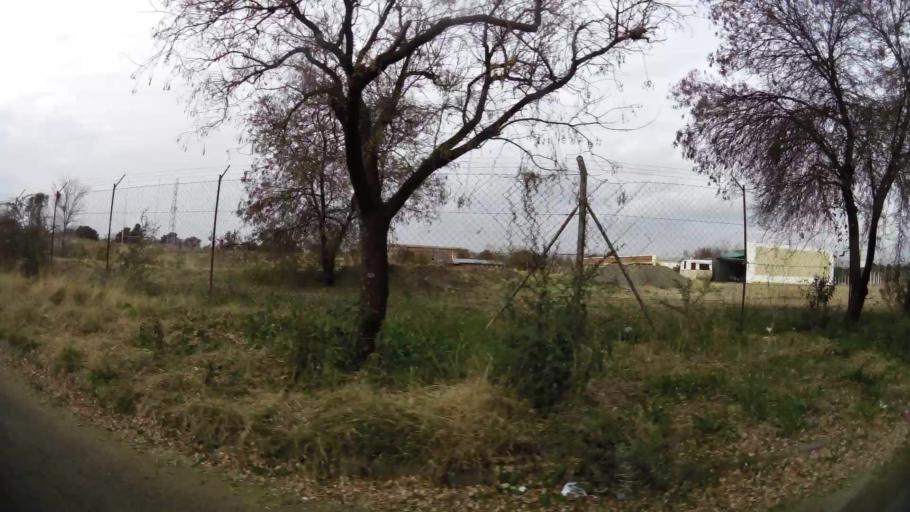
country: ZA
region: Orange Free State
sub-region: Mangaung Metropolitan Municipality
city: Bloemfontein
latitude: -29.1230
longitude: 26.1920
